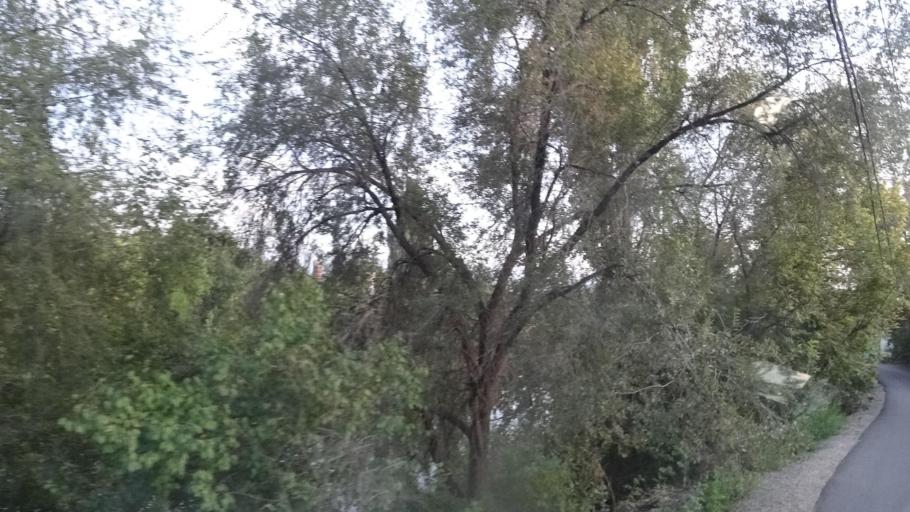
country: KZ
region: Almaty Oblysy
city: Pervomayskiy
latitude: 43.3388
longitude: 76.9979
